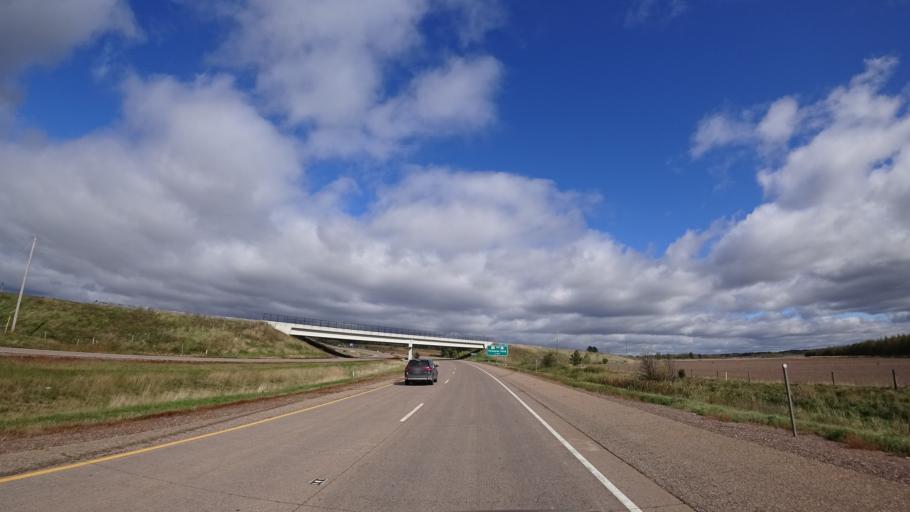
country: US
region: Wisconsin
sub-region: Chippewa County
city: Chippewa Falls
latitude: 44.8998
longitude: -91.3768
